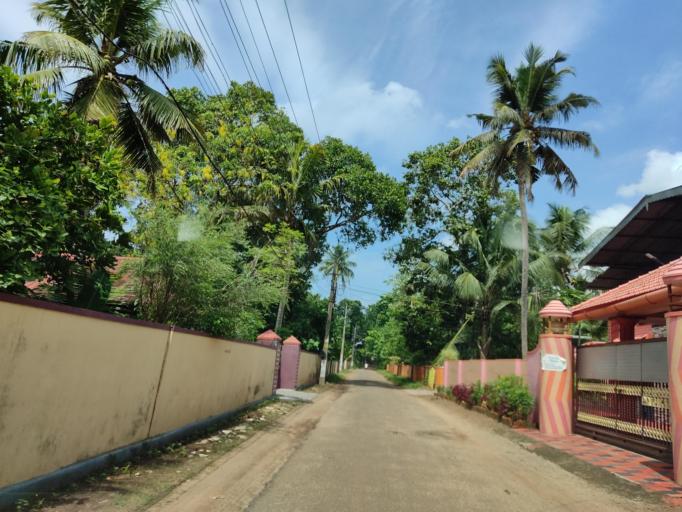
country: IN
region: Kerala
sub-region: Alappuzha
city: Mavelikara
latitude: 9.2605
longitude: 76.5610
